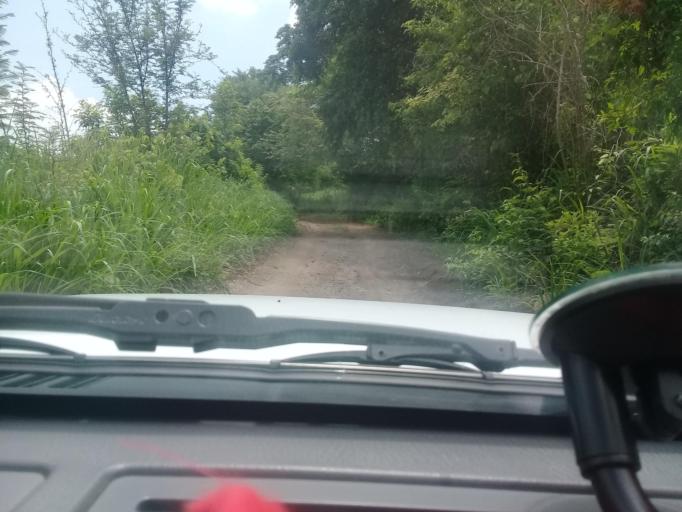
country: MX
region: Veracruz
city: Paso de Ovejas
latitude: 19.2851
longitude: -96.4272
